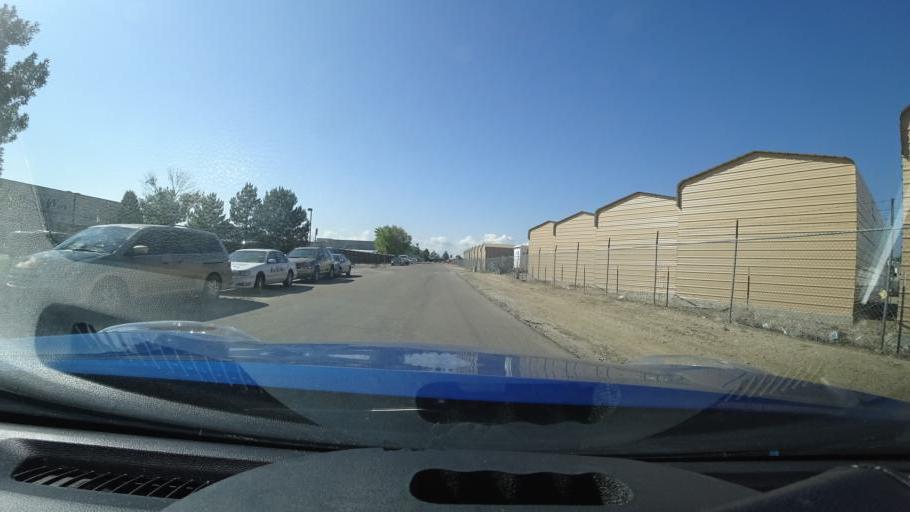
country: US
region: Colorado
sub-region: Adams County
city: Aurora
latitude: 39.7207
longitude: -104.7959
